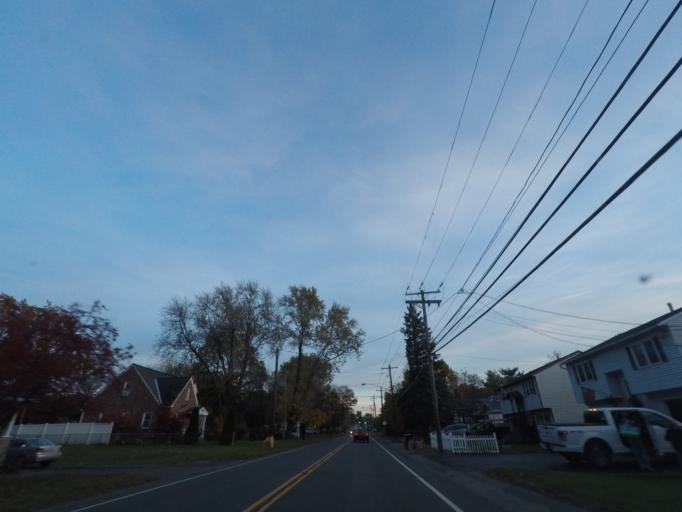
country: US
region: New York
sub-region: Schenectady County
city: Rotterdam
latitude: 42.7767
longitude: -73.9537
